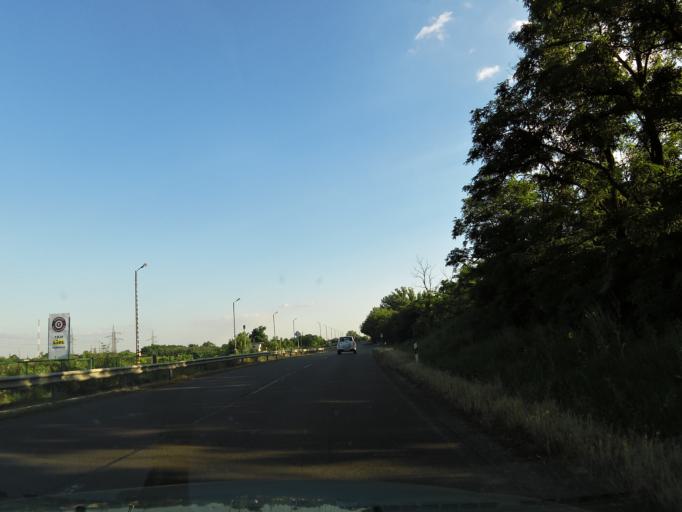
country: HU
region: Jasz-Nagykun-Szolnok
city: Rakocziujfalu
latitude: 47.0279
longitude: 20.2940
